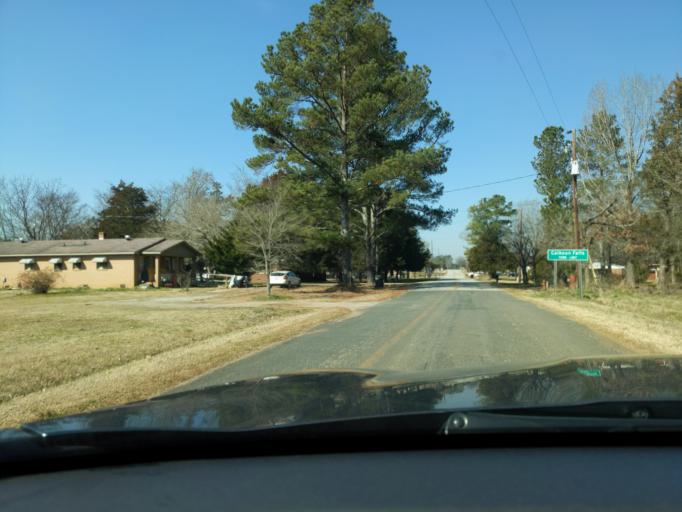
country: US
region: South Carolina
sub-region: Abbeville County
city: Calhoun Falls
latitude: 34.0849
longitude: -82.5808
